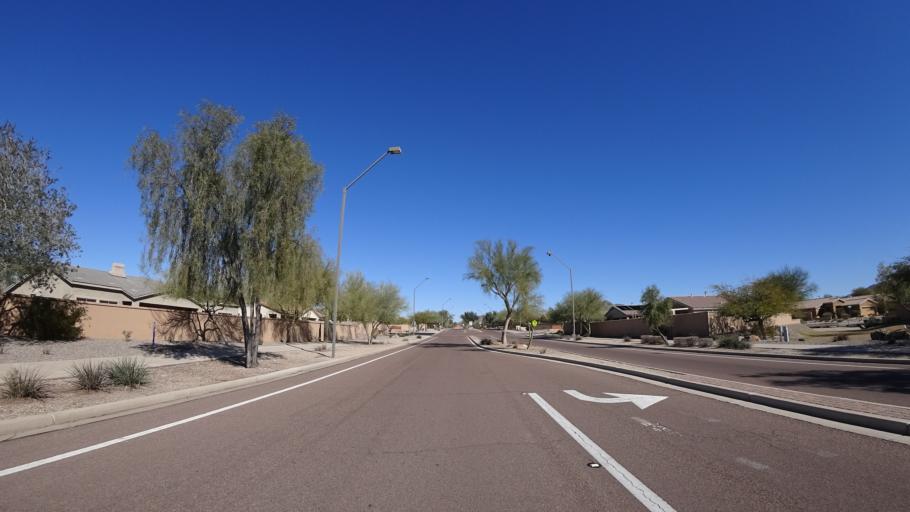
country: US
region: Arizona
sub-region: Maricopa County
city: Goodyear
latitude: 33.3285
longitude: -112.4300
